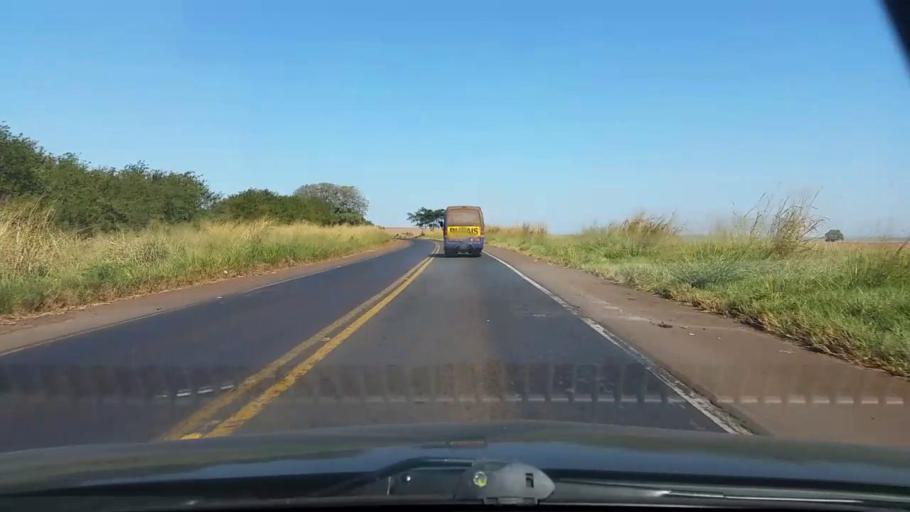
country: BR
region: Sao Paulo
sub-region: Igaracu Do Tiete
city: Igaracu do Tiete
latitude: -22.5637
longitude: -48.5636
